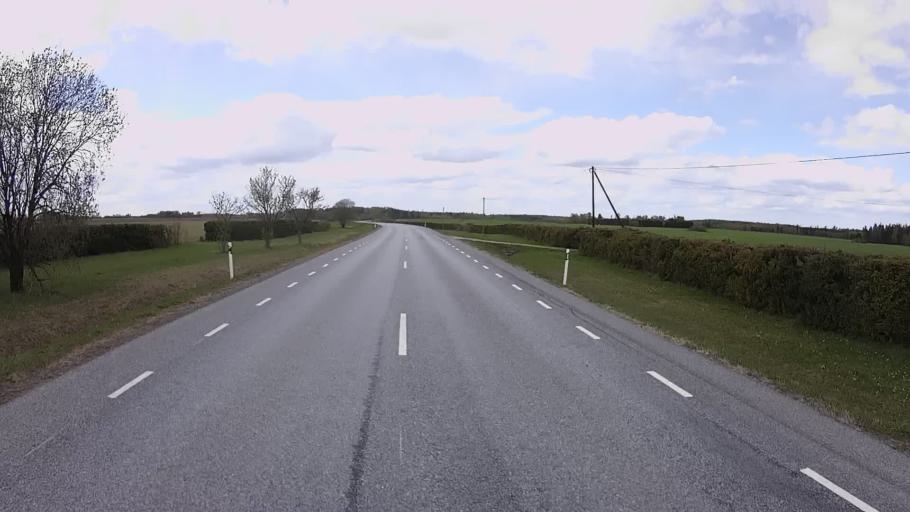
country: EE
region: Jaervamaa
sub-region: Koeru vald
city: Koeru
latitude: 58.9869
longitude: 26.0015
